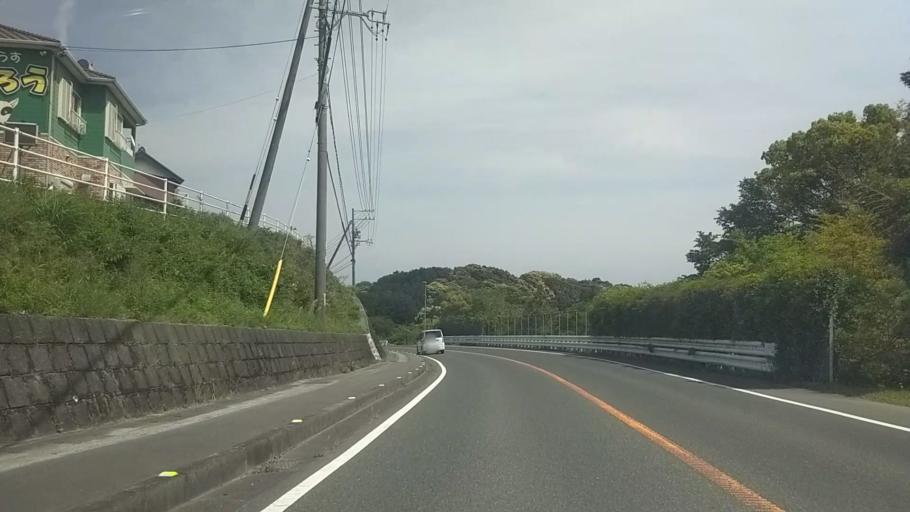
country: JP
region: Shizuoka
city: Kosai-shi
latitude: 34.7886
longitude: 137.5904
